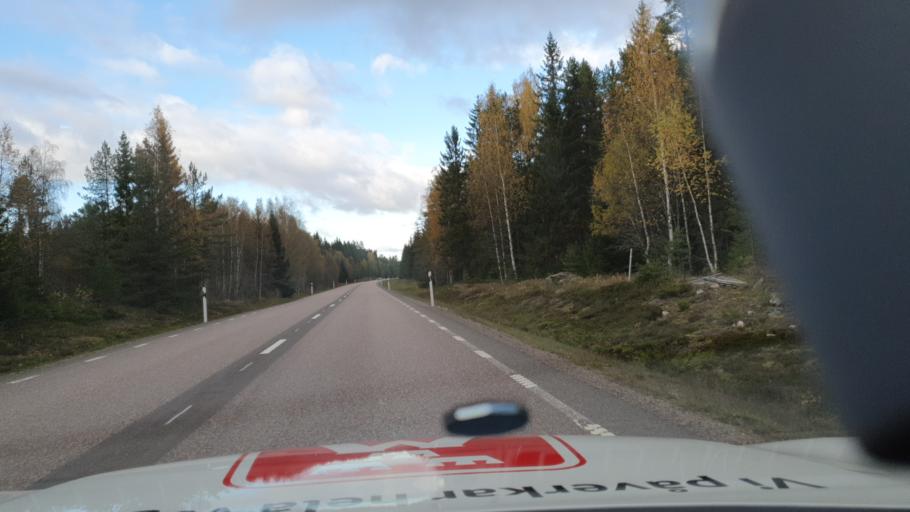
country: SE
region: Gaevleborg
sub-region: Gavle Kommun
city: Hedesunda
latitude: 60.3682
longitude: 16.9684
